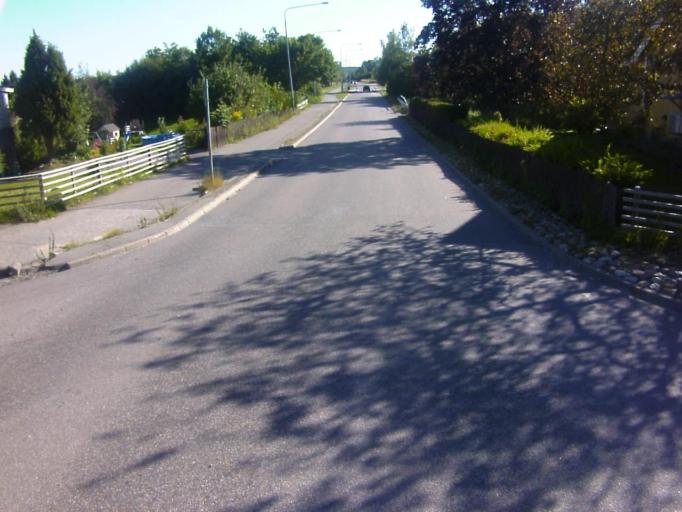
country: SE
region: Soedermanland
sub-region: Eskilstuna Kommun
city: Hallbybrunn
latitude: 59.3908
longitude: 16.4183
